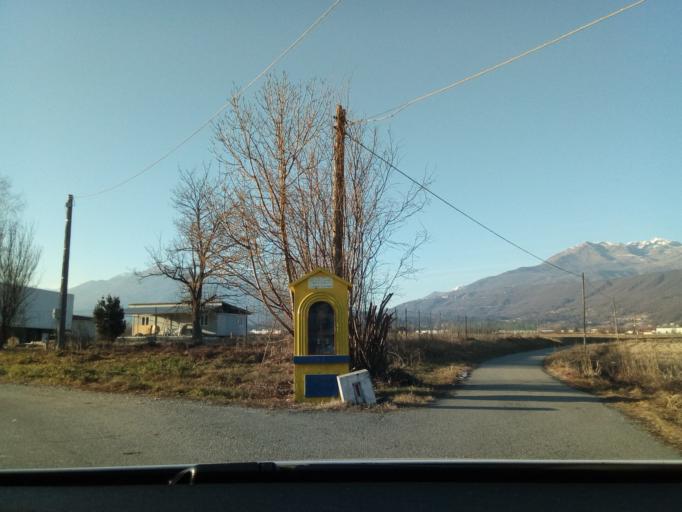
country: IT
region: Piedmont
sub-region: Provincia di Torino
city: Bollengo
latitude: 45.4631
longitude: 7.9334
